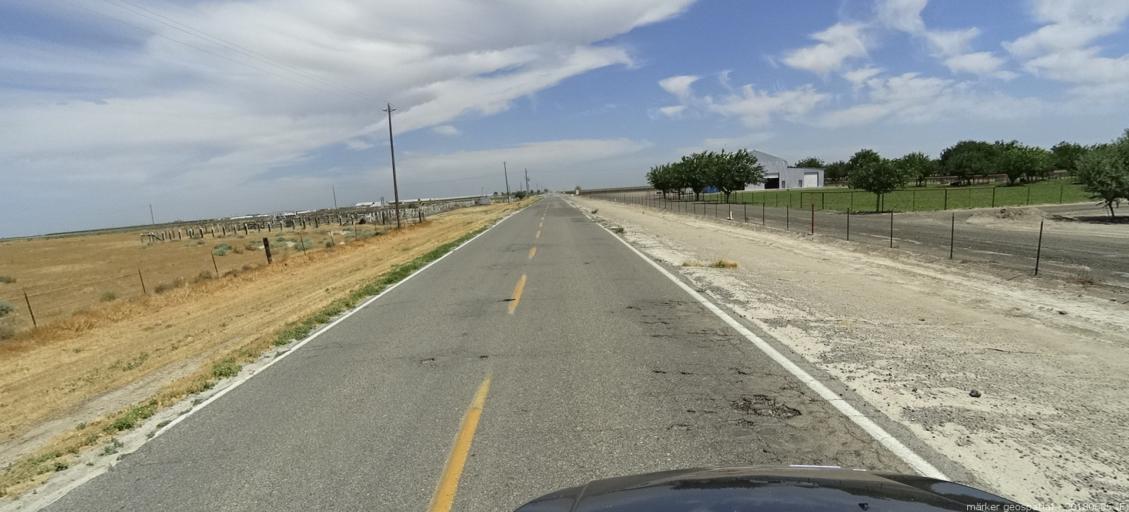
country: US
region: California
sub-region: Fresno County
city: Firebaugh
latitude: 36.9209
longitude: -120.3821
